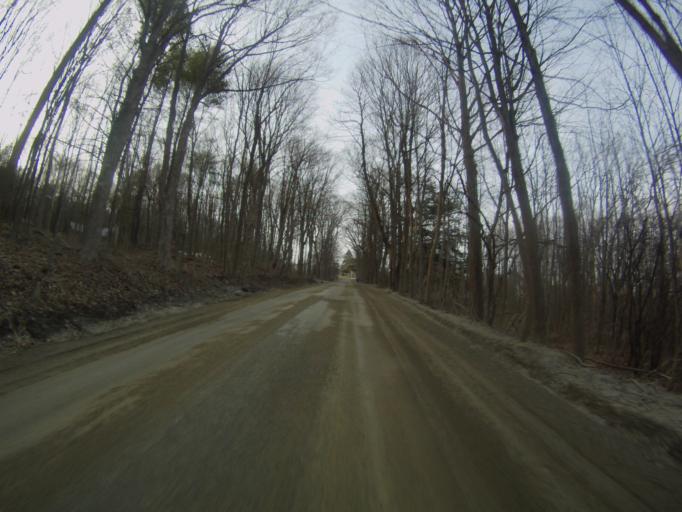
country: US
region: Vermont
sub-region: Addison County
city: Middlebury (village)
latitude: 44.0241
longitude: -73.2592
